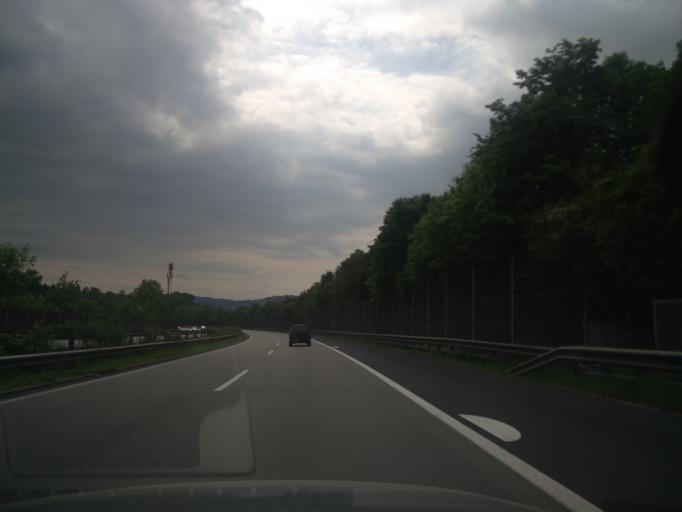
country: AT
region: Upper Austria
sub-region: Politischer Bezirk Urfahr-Umgebung
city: Altenberg bei Linz
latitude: 48.3377
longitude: 14.3356
